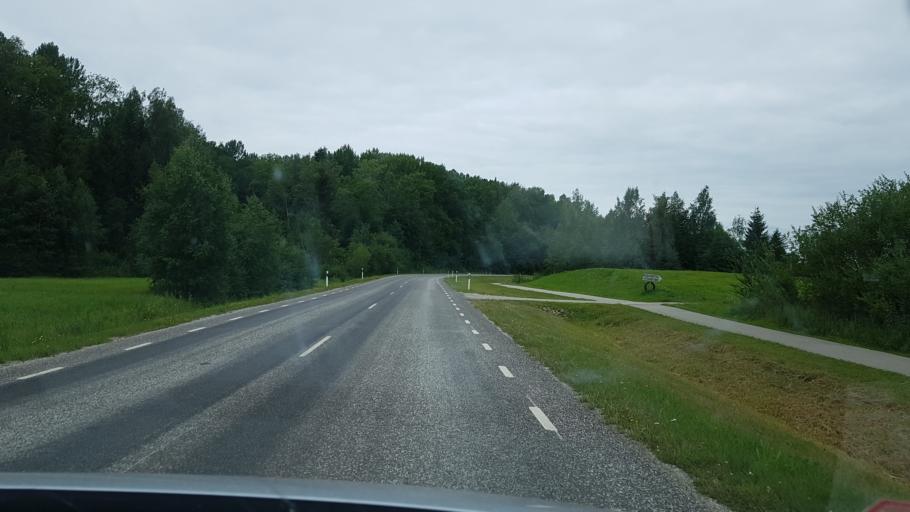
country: EE
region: Vorumaa
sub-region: Antsla vald
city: Vana-Antsla
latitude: 58.0442
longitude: 26.5480
